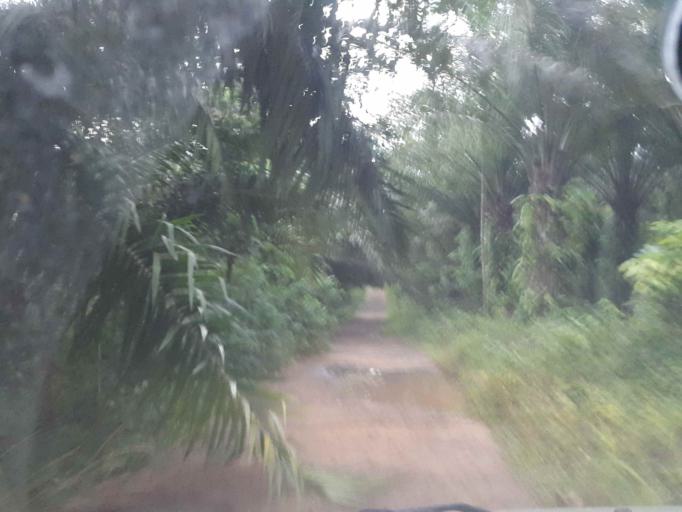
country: ID
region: Lampung
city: Sidorejo
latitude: -5.5545
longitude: 105.5235
